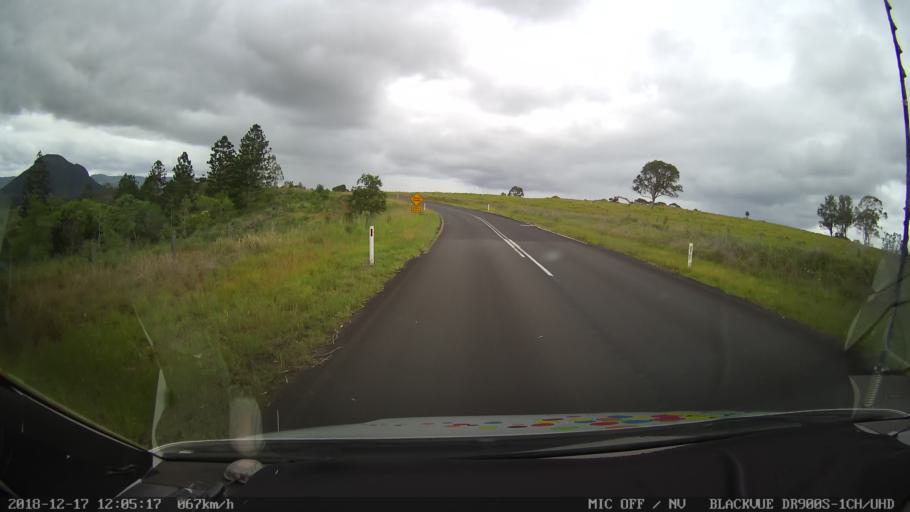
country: AU
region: New South Wales
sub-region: Kyogle
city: Kyogle
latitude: -28.4938
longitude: 152.5671
